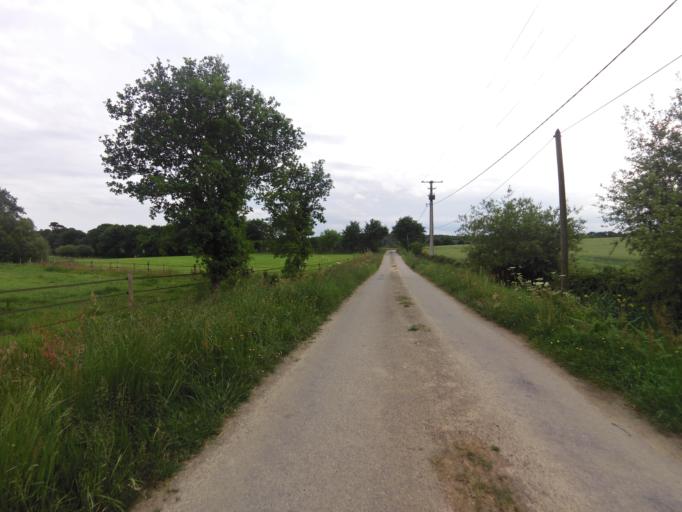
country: FR
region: Brittany
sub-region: Departement du Morbihan
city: Molac
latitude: 47.7646
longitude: -2.4232
